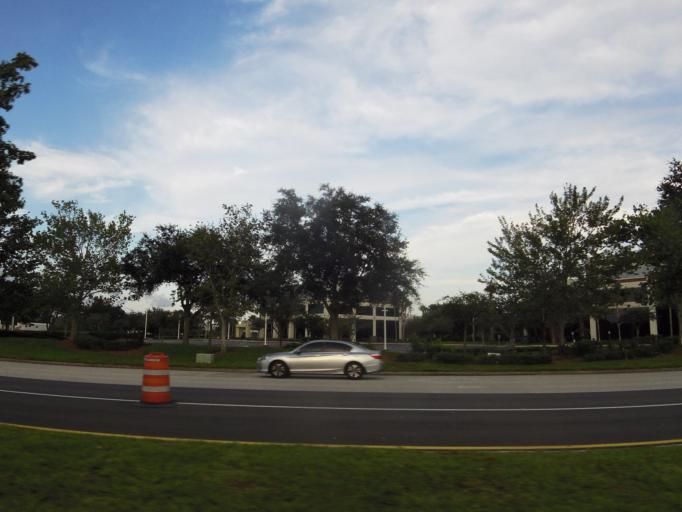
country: US
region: Florida
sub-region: Duval County
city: Jacksonville
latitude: 30.2469
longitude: -81.5360
